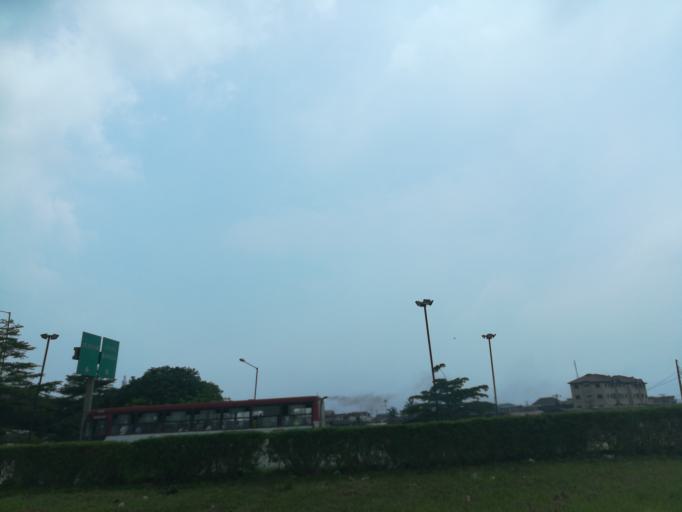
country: NG
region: Lagos
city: Somolu
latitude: 6.5468
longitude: 3.3976
